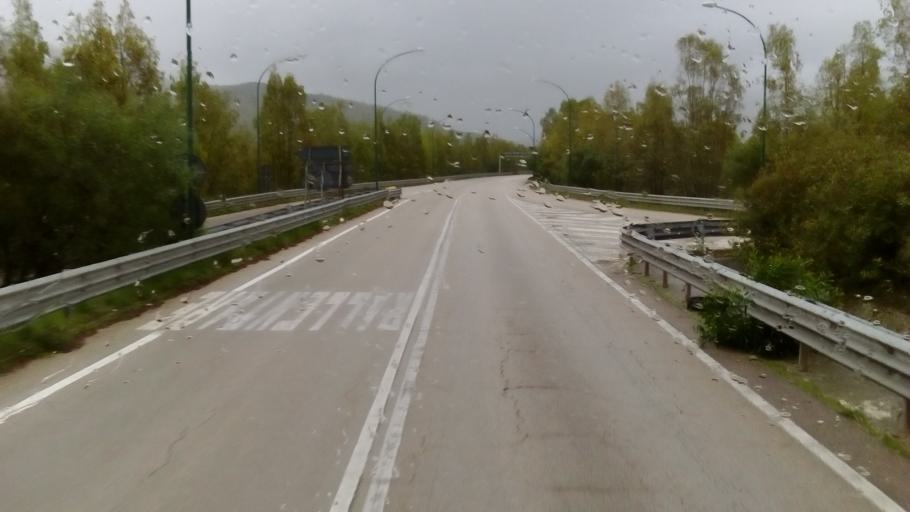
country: IT
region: Sicily
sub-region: Enna
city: Villarosa
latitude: 37.5361
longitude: 14.1293
